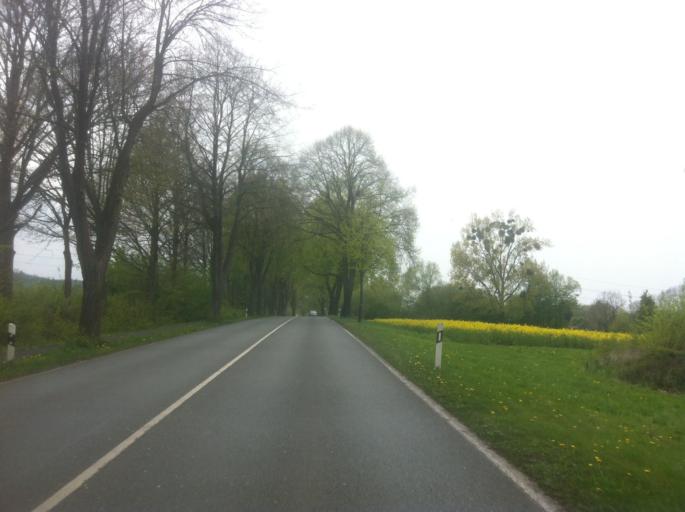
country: DE
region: North Rhine-Westphalia
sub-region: Regierungsbezirk Detmold
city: Oerlinghausen
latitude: 51.9765
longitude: 8.6619
